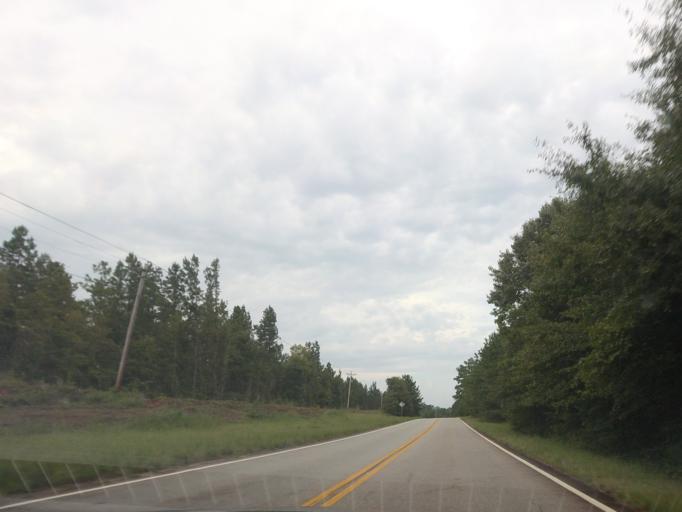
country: US
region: Georgia
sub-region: Twiggs County
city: Jeffersonville
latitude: 32.7418
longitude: -83.4265
